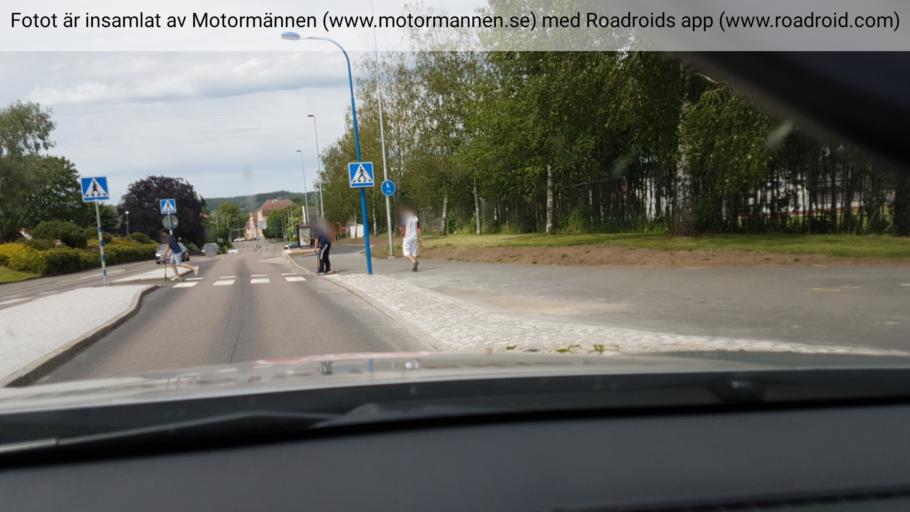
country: SE
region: Vaestra Goetaland
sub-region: Falkopings Kommun
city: Falkoeping
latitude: 58.1638
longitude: 13.5616
